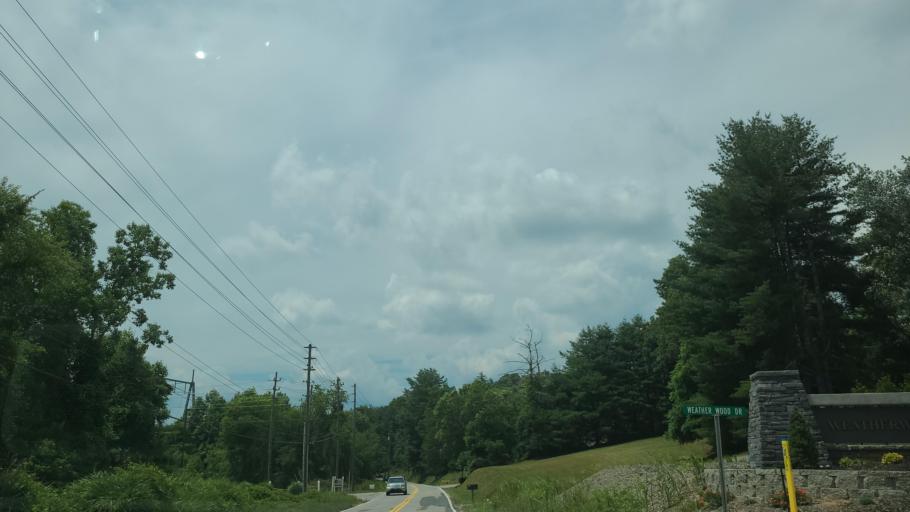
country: US
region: North Carolina
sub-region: Buncombe County
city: Avery Creek
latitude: 35.4873
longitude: -82.5727
